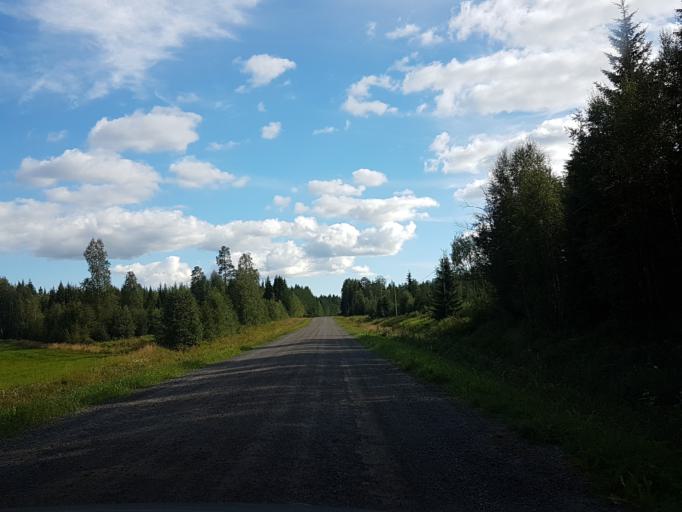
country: SE
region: Vaesterbotten
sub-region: Robertsfors Kommun
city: Robertsfors
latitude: 64.1802
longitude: 20.6447
